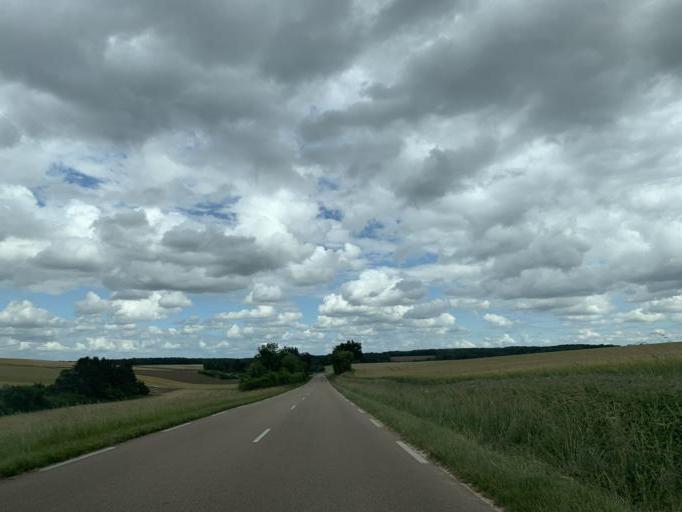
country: FR
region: Bourgogne
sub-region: Departement de l'Yonne
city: Chablis
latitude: 47.7357
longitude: 3.7838
